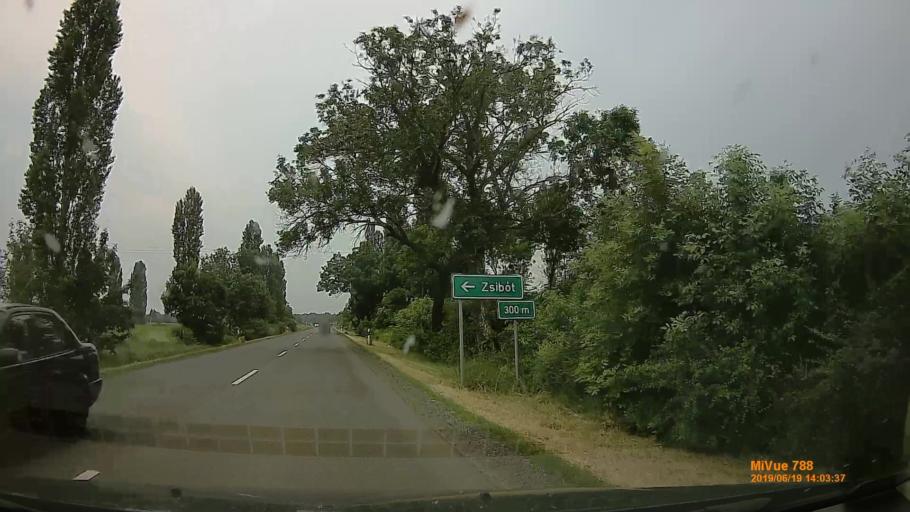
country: HU
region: Baranya
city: Szigetvar
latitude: 46.0603
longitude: 17.8118
